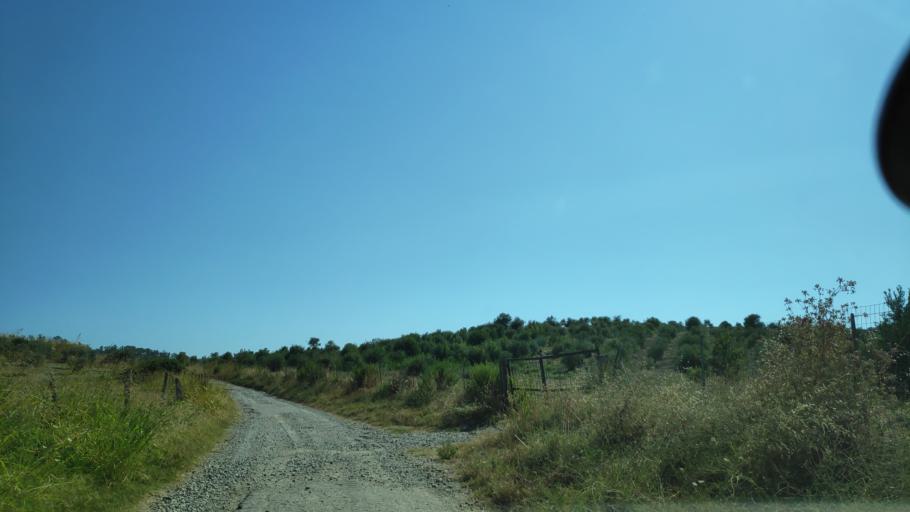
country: IT
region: Calabria
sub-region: Provincia di Reggio Calabria
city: Monasterace
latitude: 38.4335
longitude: 16.5250
